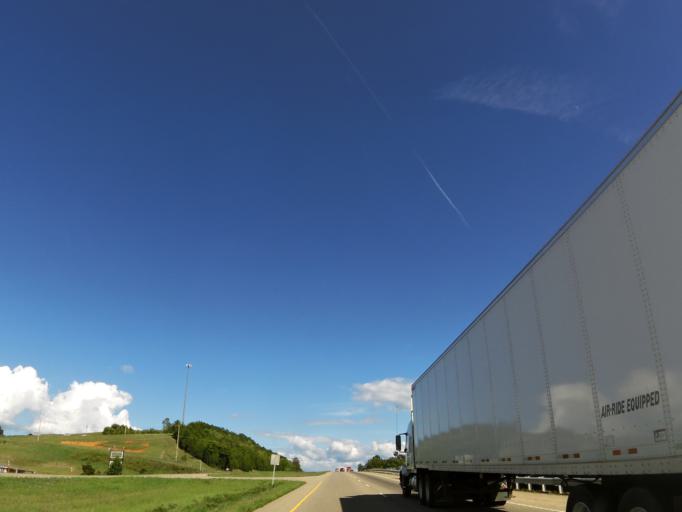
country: US
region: Tennessee
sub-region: Greene County
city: Mosheim
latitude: 36.1912
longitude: -82.9866
